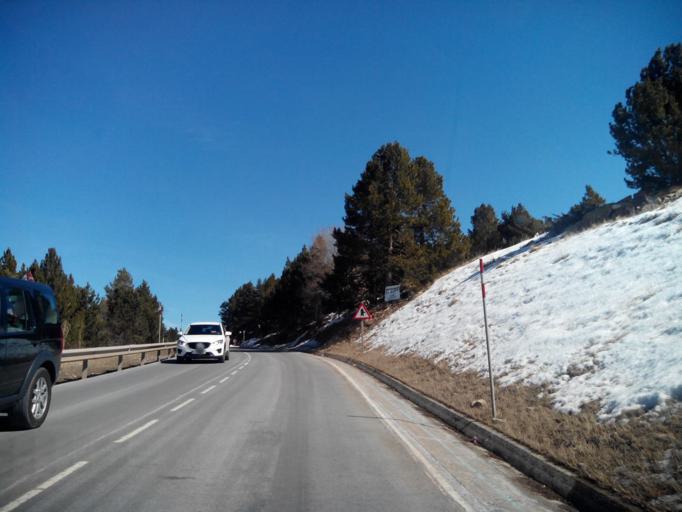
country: ES
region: Catalonia
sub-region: Provincia de Girona
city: Toses
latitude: 42.3262
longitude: 1.9587
